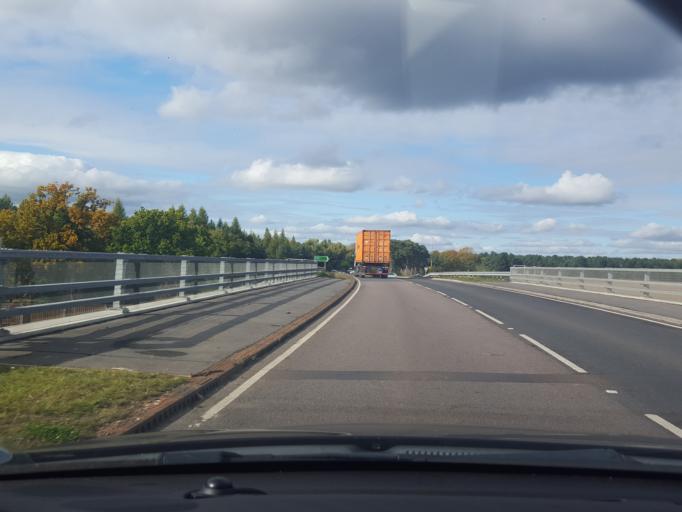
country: GB
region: England
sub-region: Norfolk
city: Thetford
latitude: 52.3885
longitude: 0.6646
